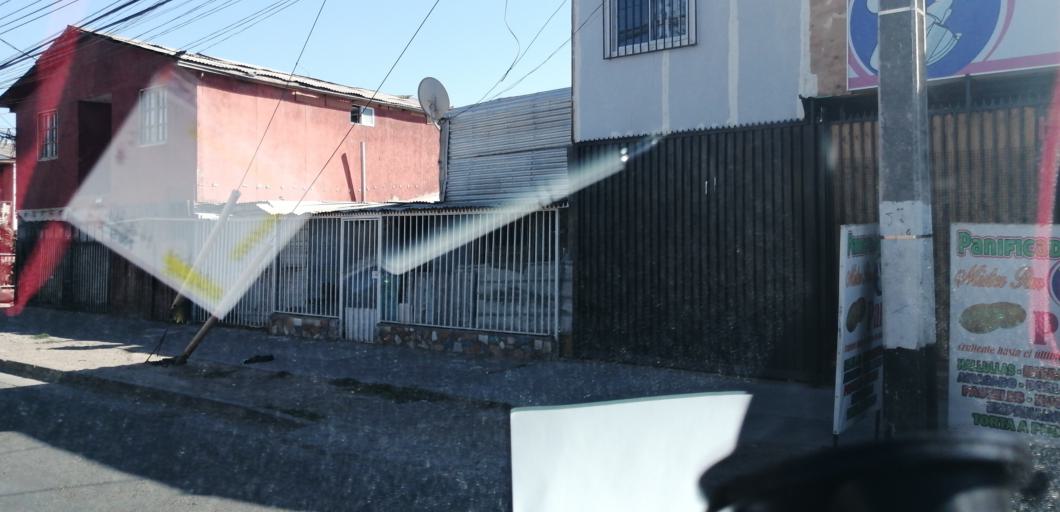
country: CL
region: Santiago Metropolitan
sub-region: Provincia de Santiago
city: Lo Prado
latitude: -33.4398
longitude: -70.7549
